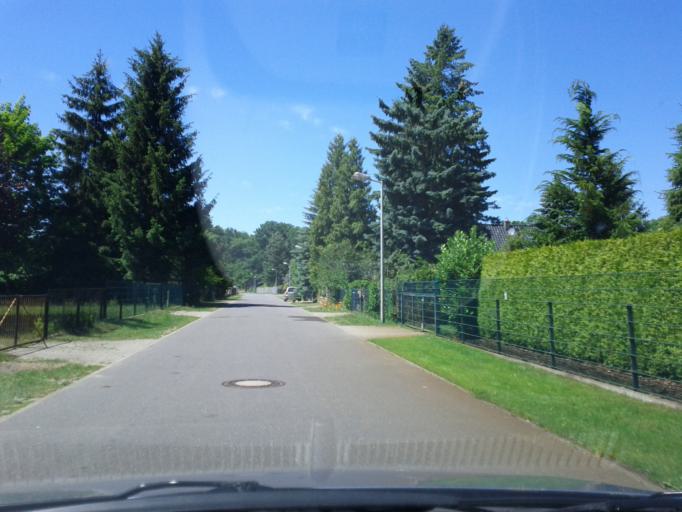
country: DE
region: Brandenburg
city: Spreenhagen
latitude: 52.3945
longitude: 13.9396
